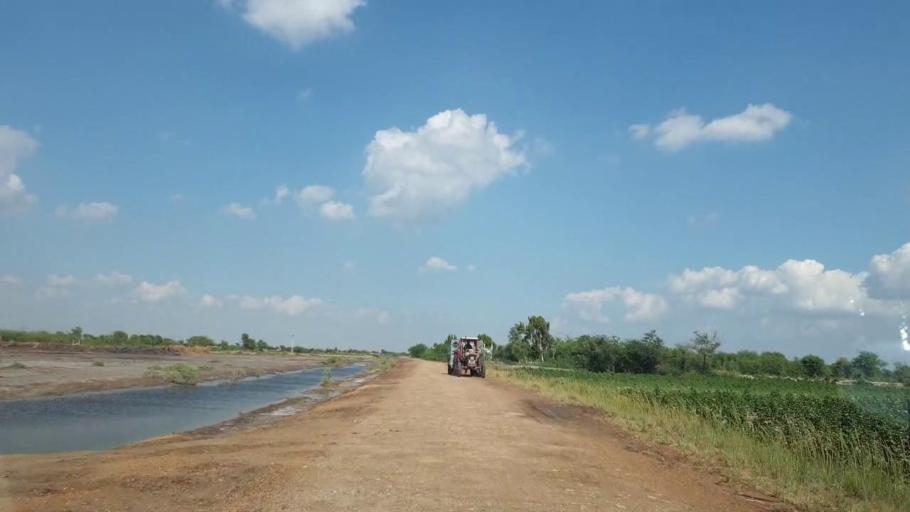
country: PK
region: Sindh
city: Pithoro
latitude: 25.6005
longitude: 69.3910
